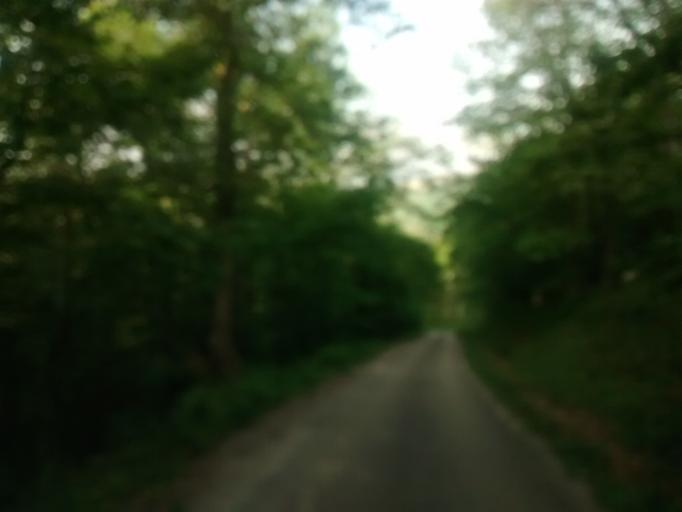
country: ES
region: Cantabria
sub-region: Provincia de Cantabria
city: Potes
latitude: 43.2405
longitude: -4.5663
